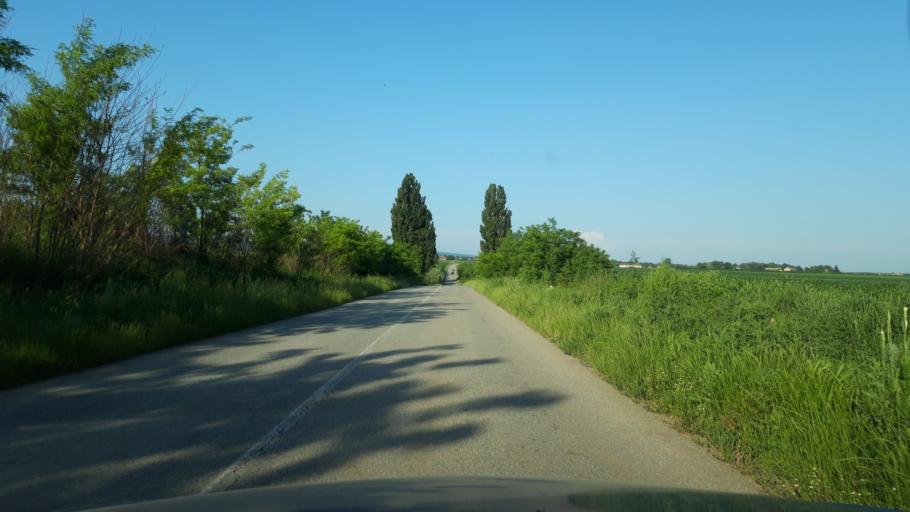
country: HR
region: Vukovarsko-Srijemska
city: Ilok
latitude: 45.1051
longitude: 19.4810
